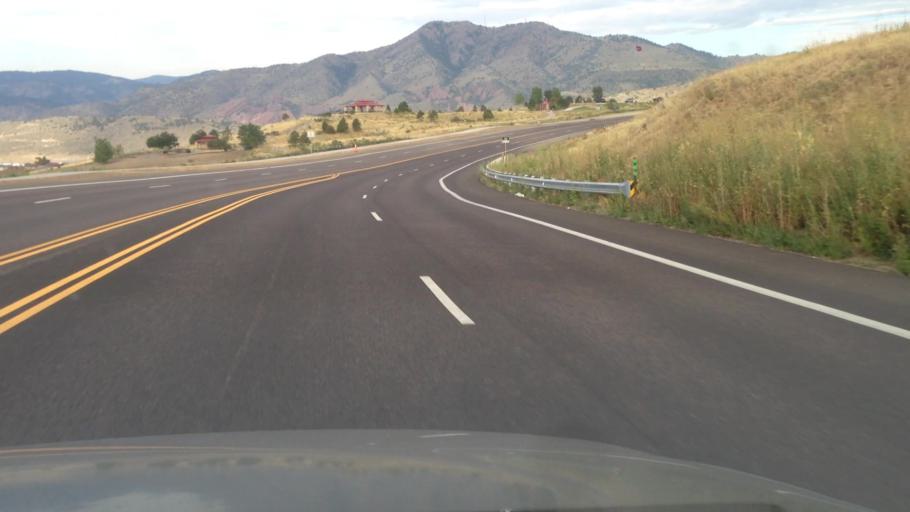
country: US
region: Colorado
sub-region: Jefferson County
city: West Pleasant View
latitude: 39.6806
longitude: -105.1643
